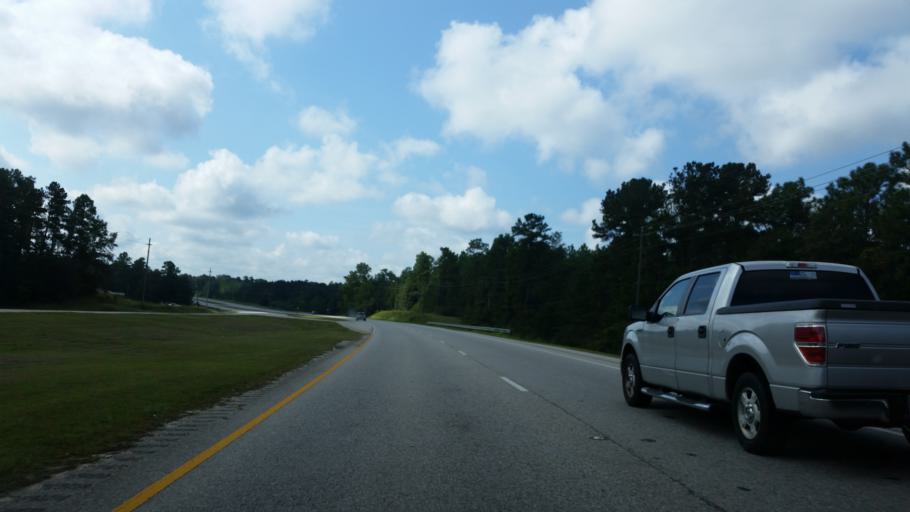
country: US
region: Alabama
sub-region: Baldwin County
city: Bay Minette
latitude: 30.9047
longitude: -87.7935
